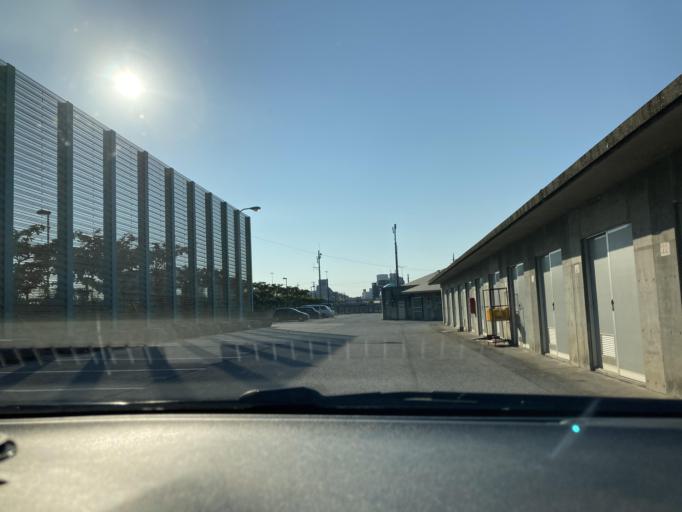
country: JP
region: Okinawa
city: Naha-shi
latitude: 26.2206
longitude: 127.6633
